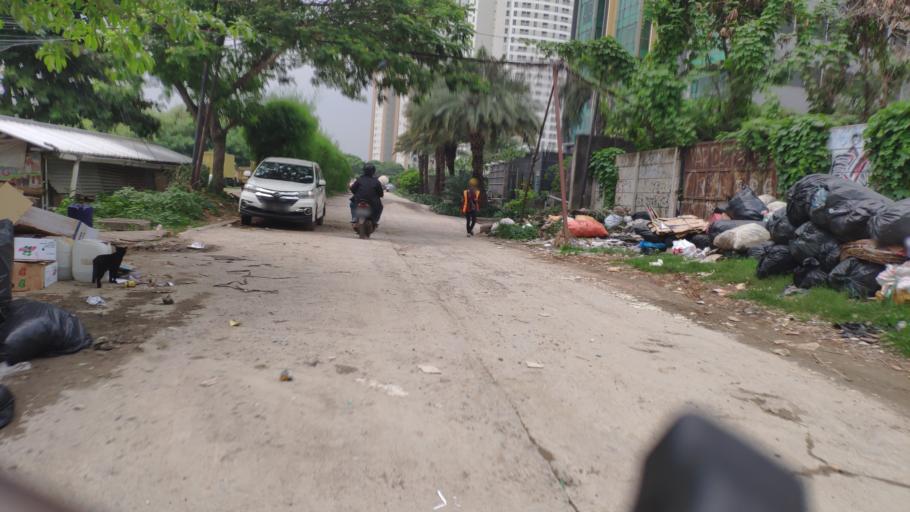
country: ID
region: Jakarta Raya
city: Jakarta
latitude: -6.2118
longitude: 106.8356
